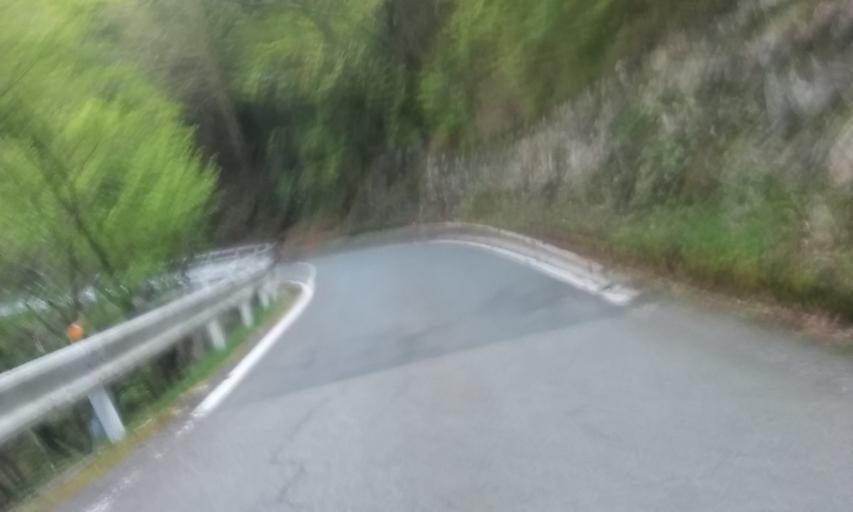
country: JP
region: Ehime
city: Saijo
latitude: 33.8026
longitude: 133.2739
